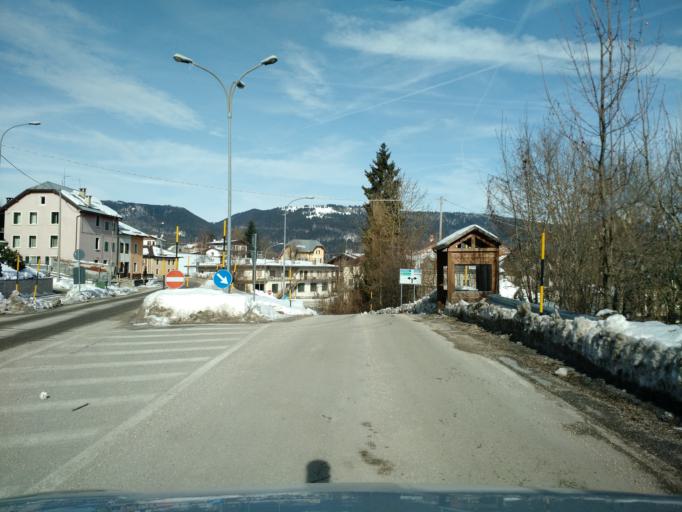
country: IT
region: Veneto
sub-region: Provincia di Vicenza
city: Roana
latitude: 45.8422
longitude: 11.4383
